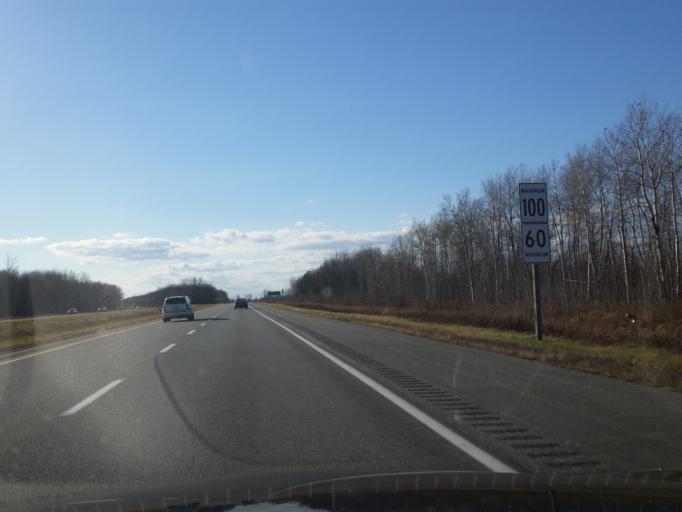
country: CA
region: Quebec
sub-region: Mauricie
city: Louiseville
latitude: 46.2137
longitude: -72.9675
